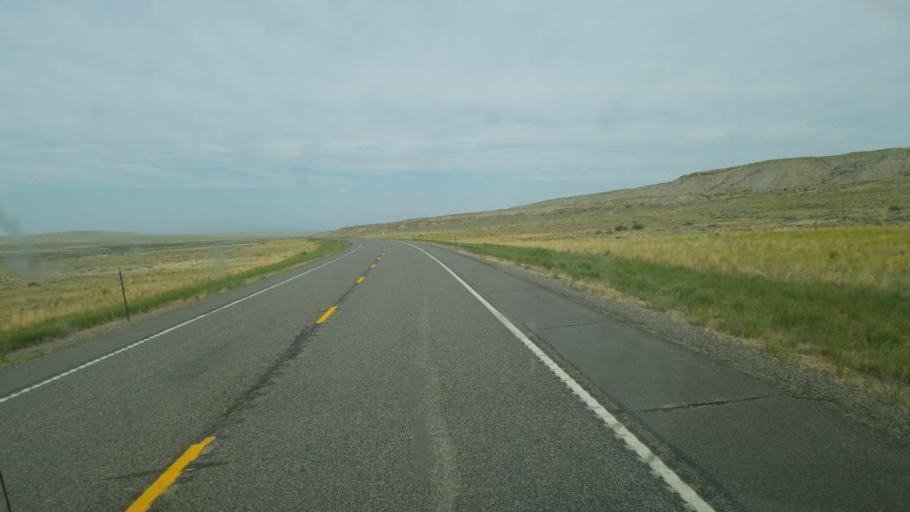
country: US
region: Wyoming
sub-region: Fremont County
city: Riverton
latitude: 43.2221
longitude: -107.9779
